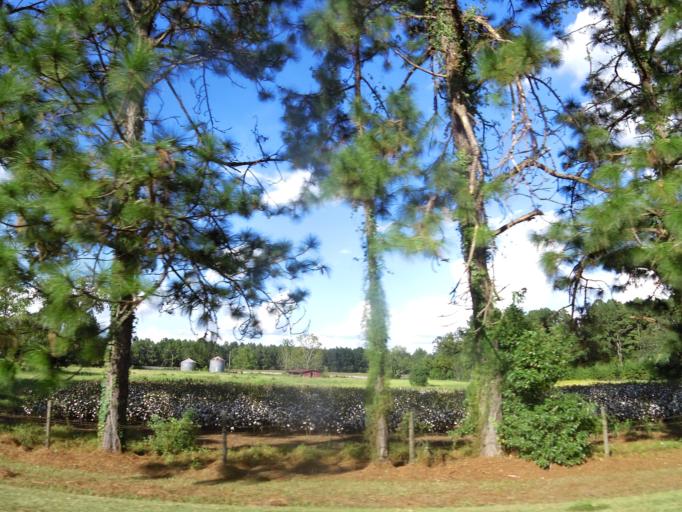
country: US
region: Georgia
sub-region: Brooks County
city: Quitman
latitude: 30.7819
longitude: -83.6208
